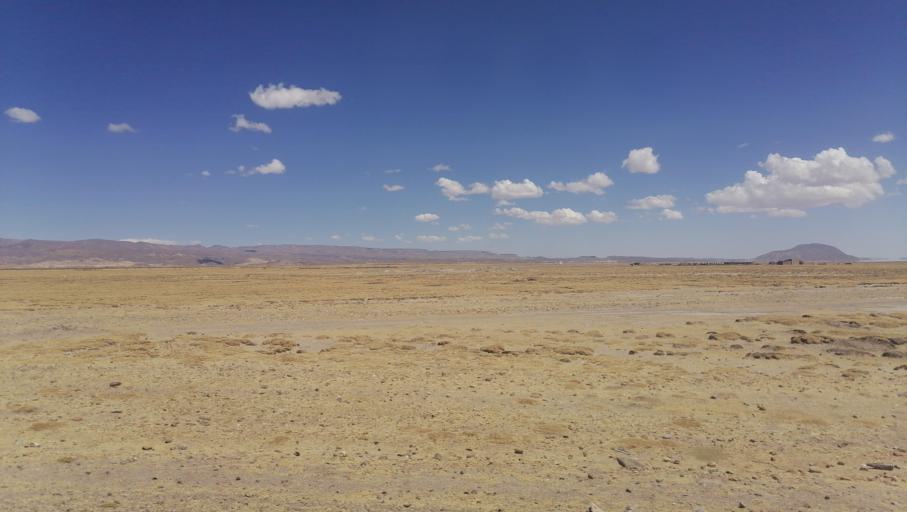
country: BO
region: Oruro
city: Challapata
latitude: -19.1724
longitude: -66.8037
